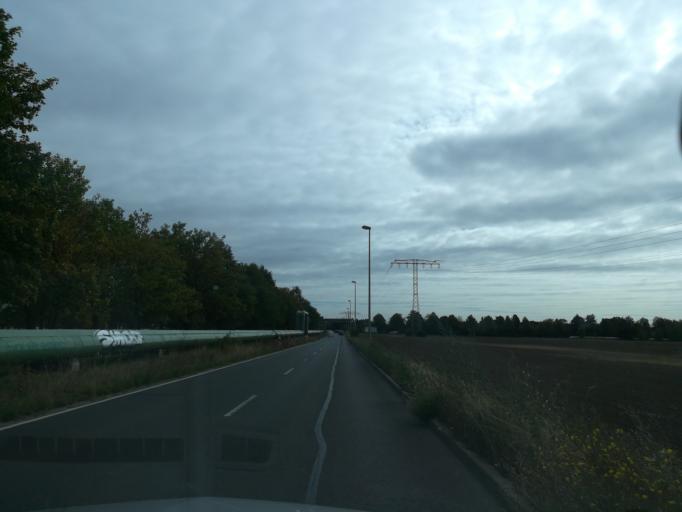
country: DE
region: Saxony-Anhalt
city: Neue Neustadt
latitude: 52.1609
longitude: 11.6016
